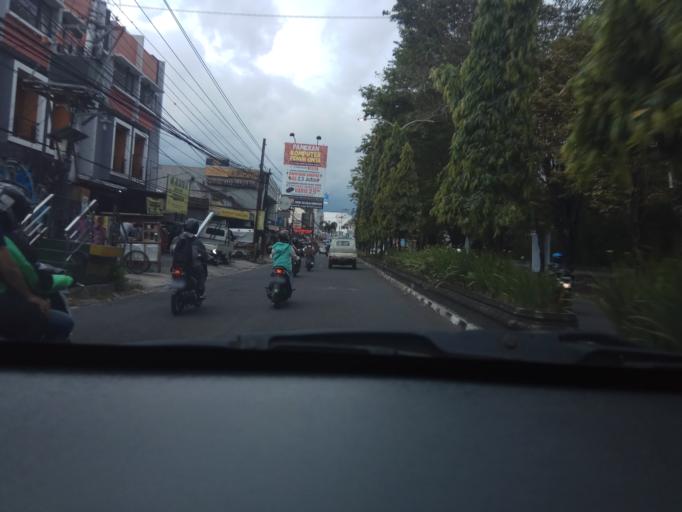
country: ID
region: Daerah Istimewa Yogyakarta
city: Yogyakarta
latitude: -7.7665
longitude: 110.3919
